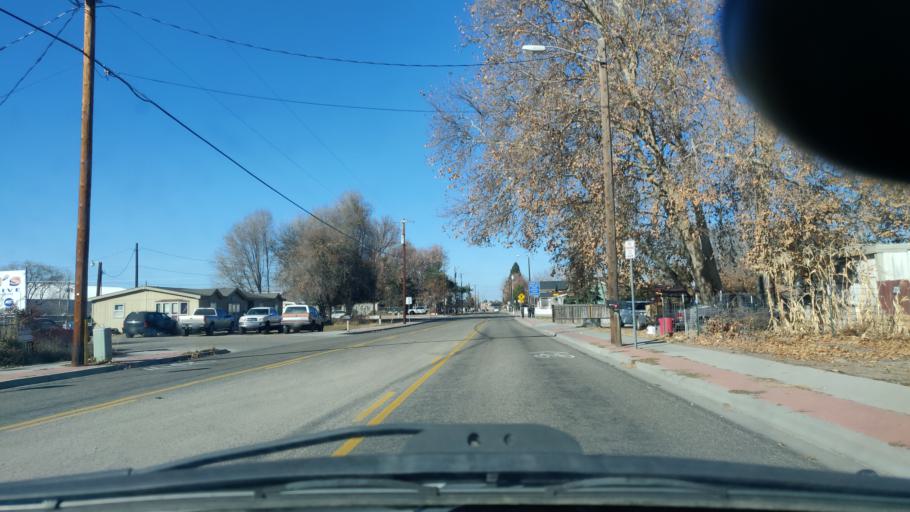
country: US
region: Idaho
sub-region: Ada County
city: Garden City
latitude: 43.6450
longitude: -116.2623
